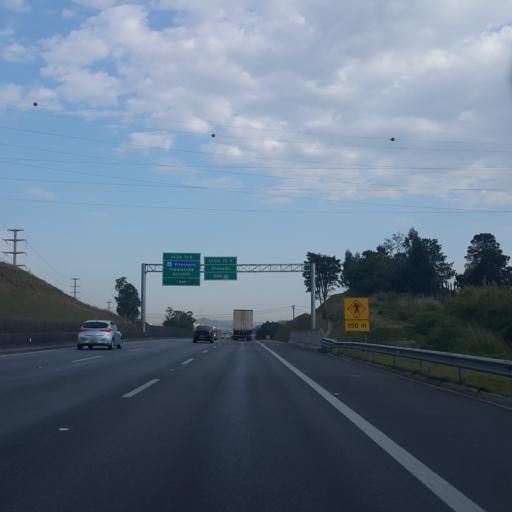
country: BR
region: Sao Paulo
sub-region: Louveira
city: Louveira
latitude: -23.0702
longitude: -46.9870
